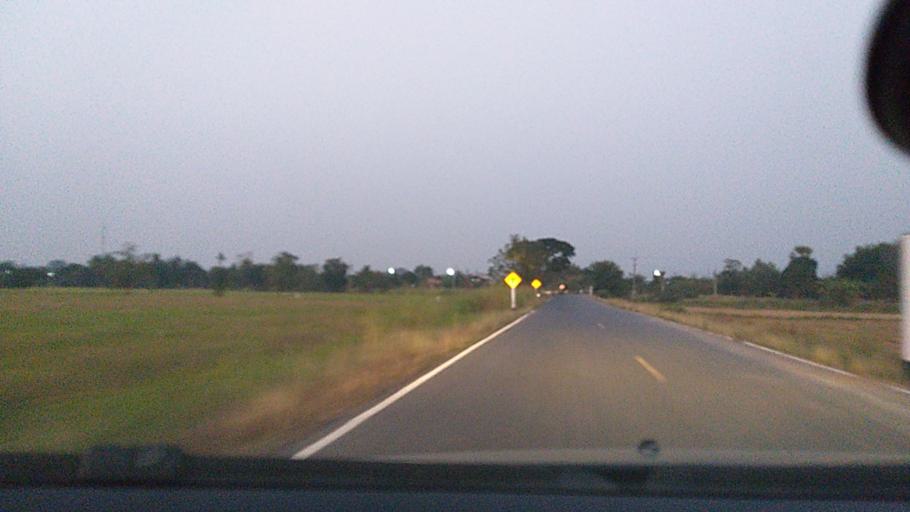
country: TH
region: Sing Buri
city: Phrom Buri
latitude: 14.8227
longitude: 100.4059
